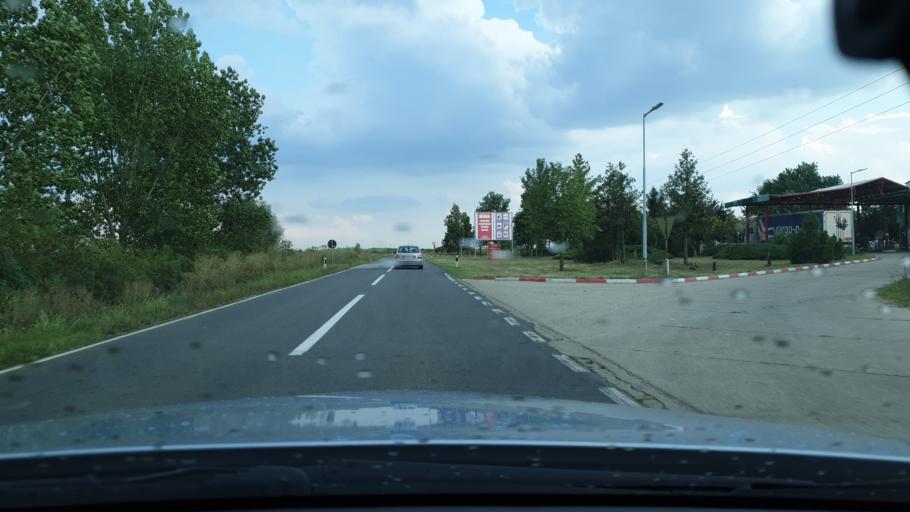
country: RS
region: Autonomna Pokrajina Vojvodina
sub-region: Srednjebanatski Okrug
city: Secanj
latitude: 45.3512
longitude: 20.7743
